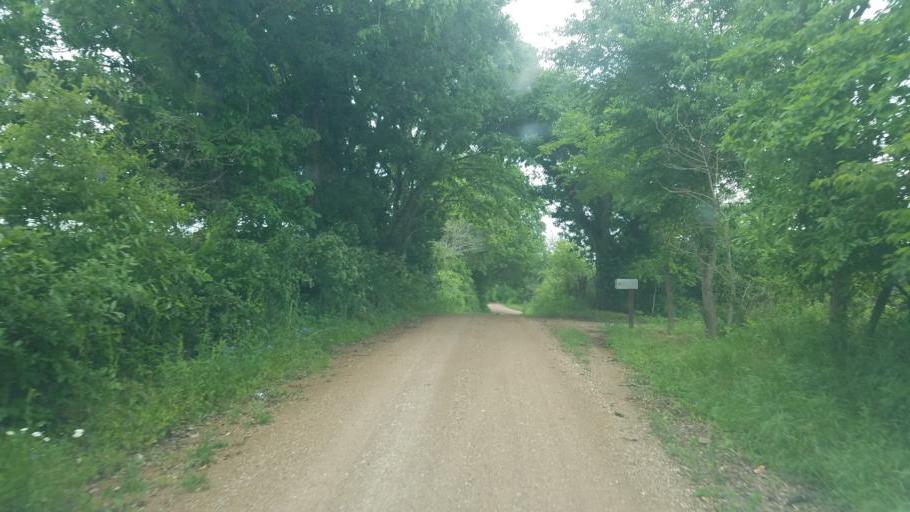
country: US
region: Missouri
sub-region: Moniteau County
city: California
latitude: 38.6211
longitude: -92.6373
